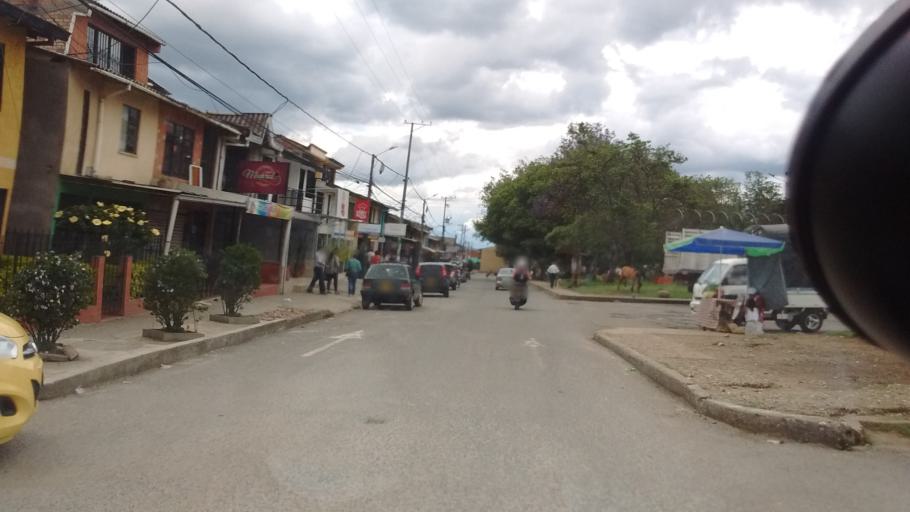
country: CO
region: Cauca
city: Popayan
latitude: 2.4768
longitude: -76.5599
